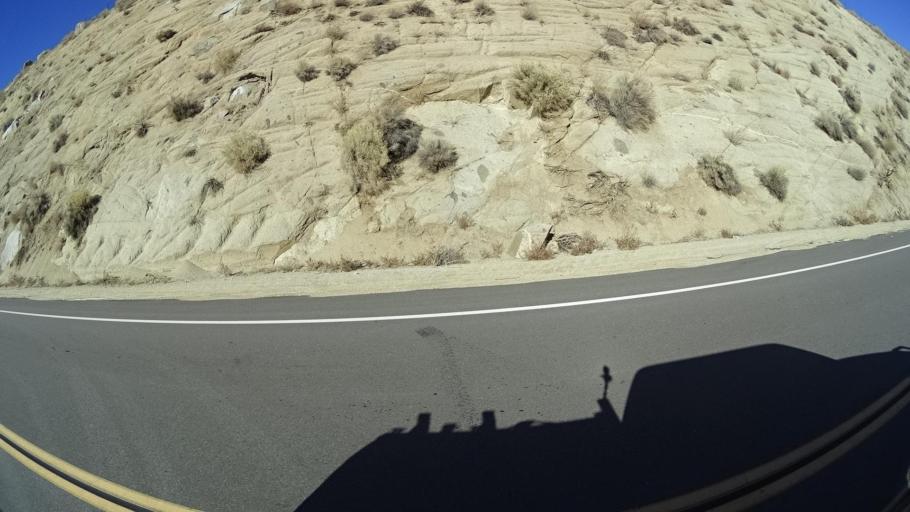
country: US
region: California
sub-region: Kern County
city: Weldon
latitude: 35.6727
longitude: -118.3530
